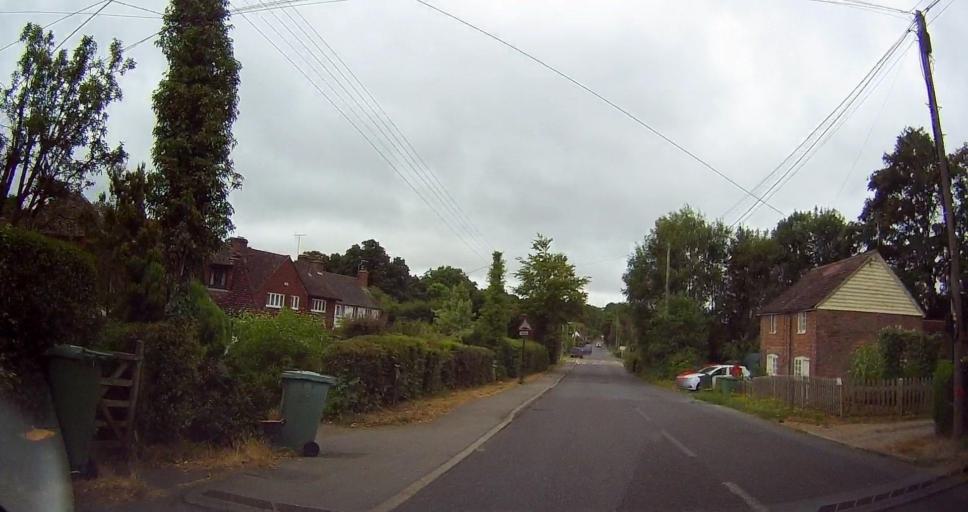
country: GB
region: England
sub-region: East Sussex
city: Wadhurst
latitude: 51.0921
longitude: 0.3873
